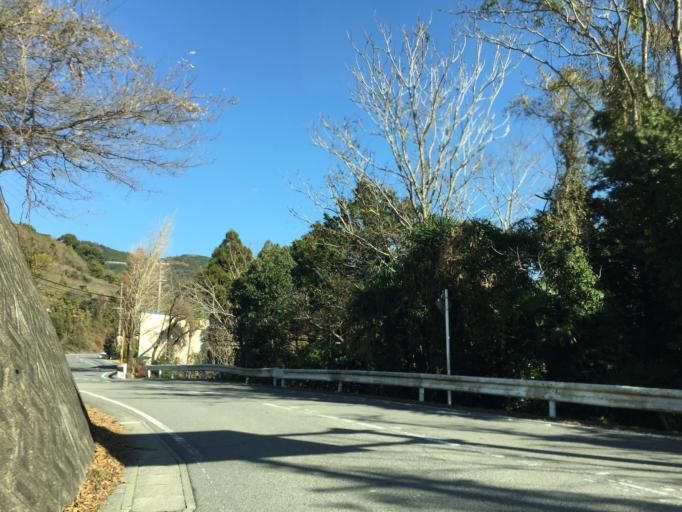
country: JP
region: Wakayama
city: Iwade
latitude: 34.1480
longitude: 135.3652
